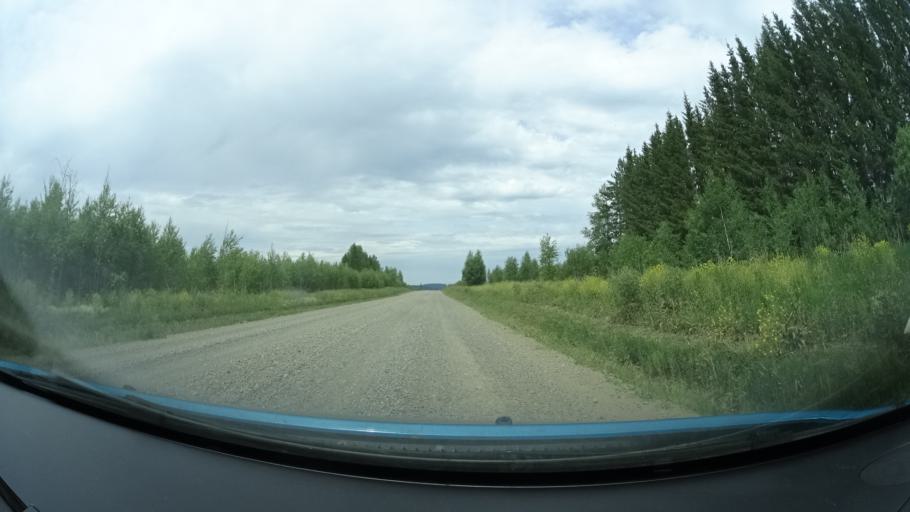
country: RU
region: Perm
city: Barda
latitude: 56.7871
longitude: 55.6735
